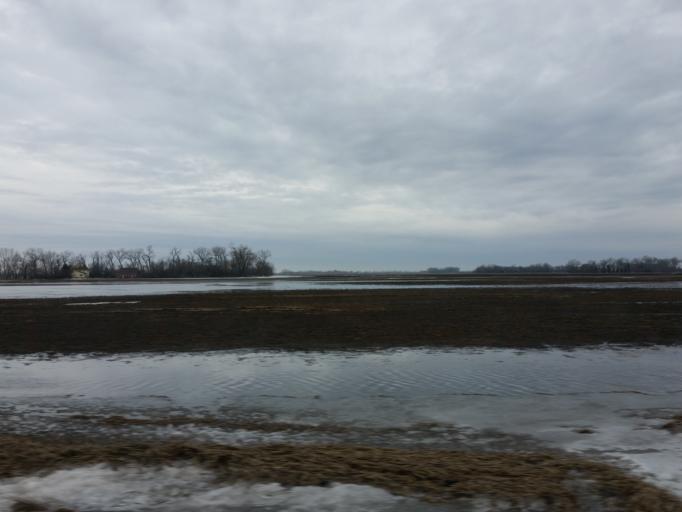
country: US
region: North Dakota
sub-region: Walsh County
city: Grafton
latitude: 48.3857
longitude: -97.4704
